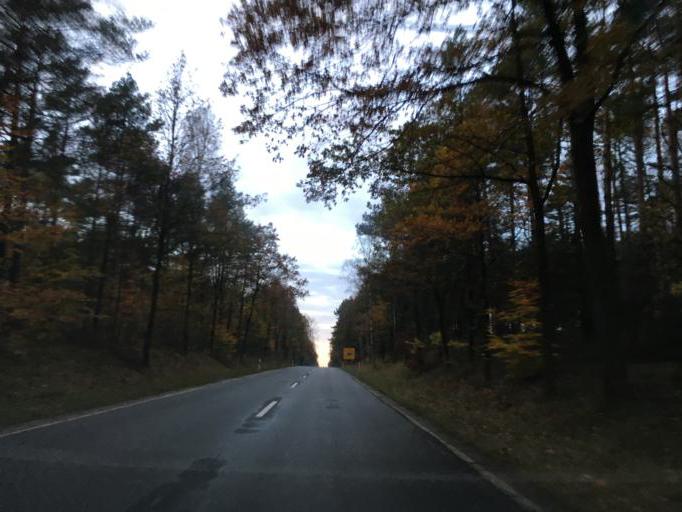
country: DE
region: Lower Saxony
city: Bispingen
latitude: 53.0686
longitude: 9.9777
